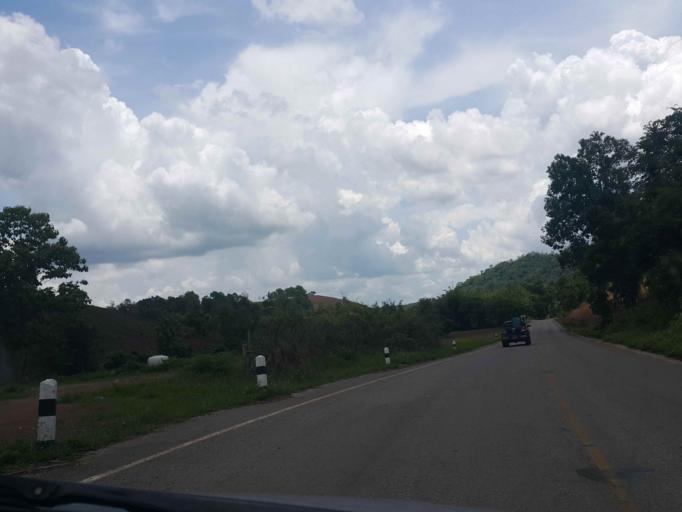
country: TH
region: Phayao
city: Chiang Muan
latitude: 18.8999
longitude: 100.1331
